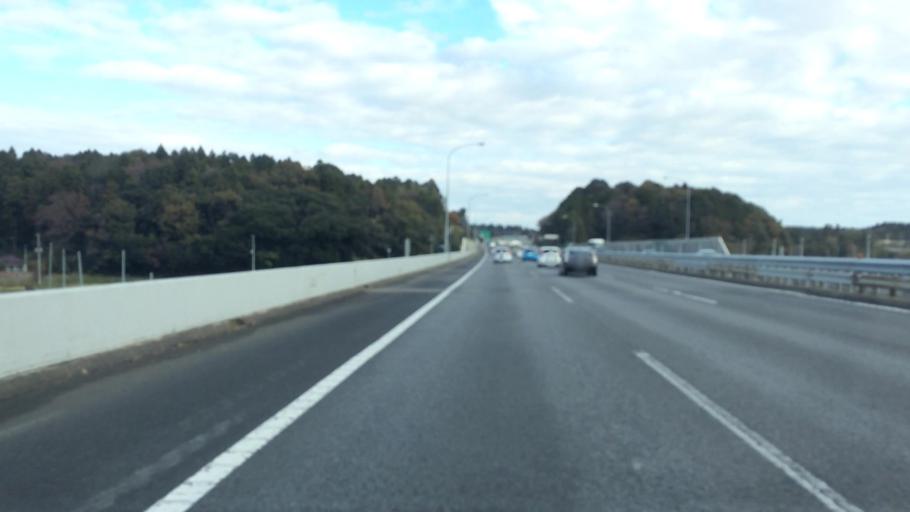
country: JP
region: Chiba
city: Shisui
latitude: 35.7176
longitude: 140.2888
